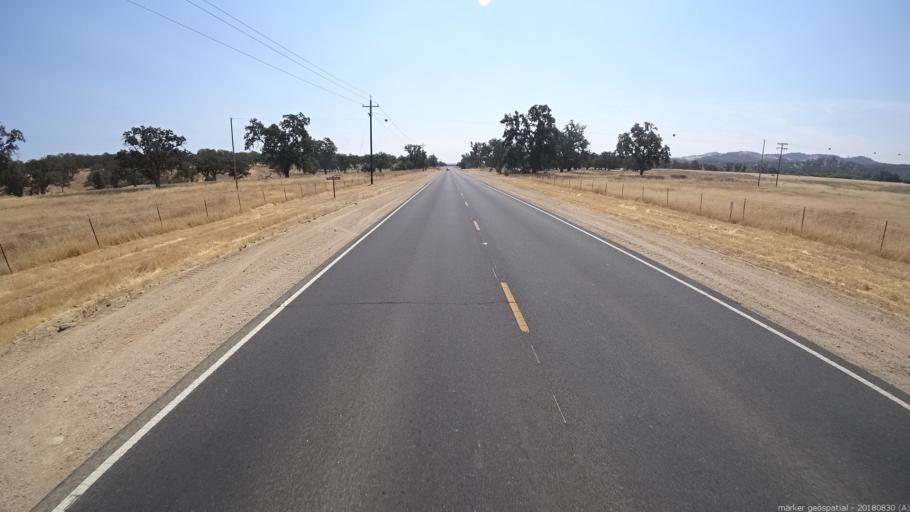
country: US
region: California
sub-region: Monterey County
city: King City
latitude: 35.9783
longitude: -121.2149
